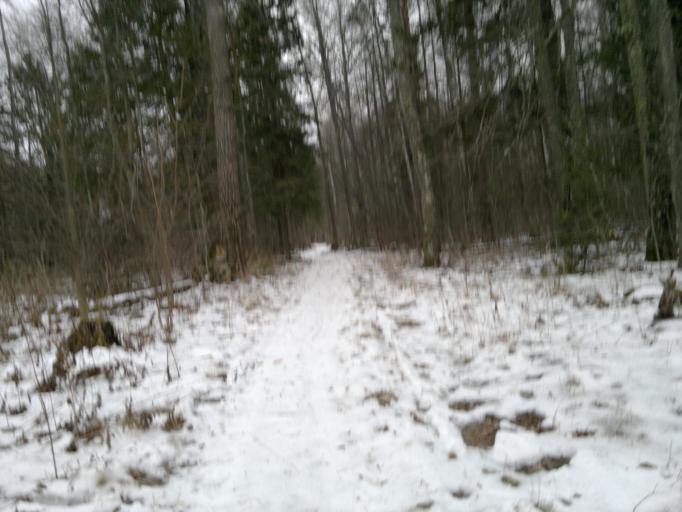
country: RU
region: Mariy-El
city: Yoshkar-Ola
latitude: 56.6097
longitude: 47.9554
